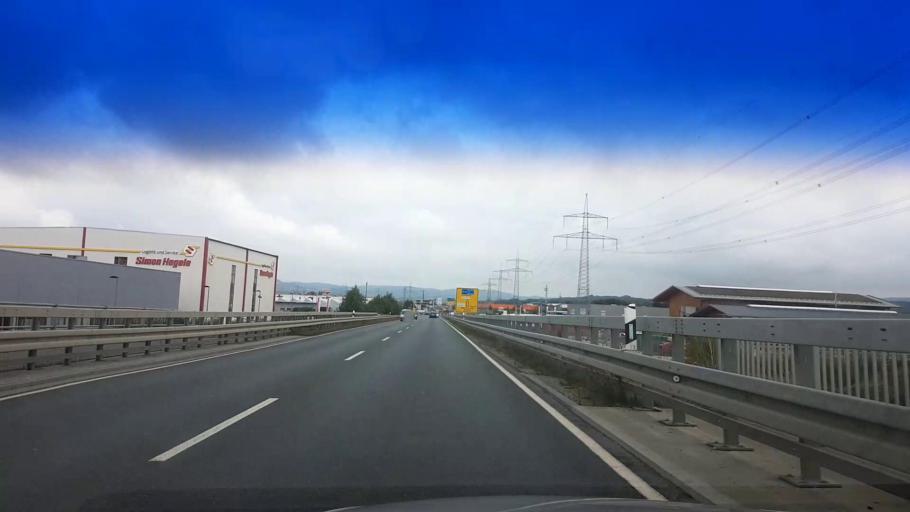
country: DE
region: Bavaria
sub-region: Upper Franconia
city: Forchheim
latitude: 49.6995
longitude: 11.0543
